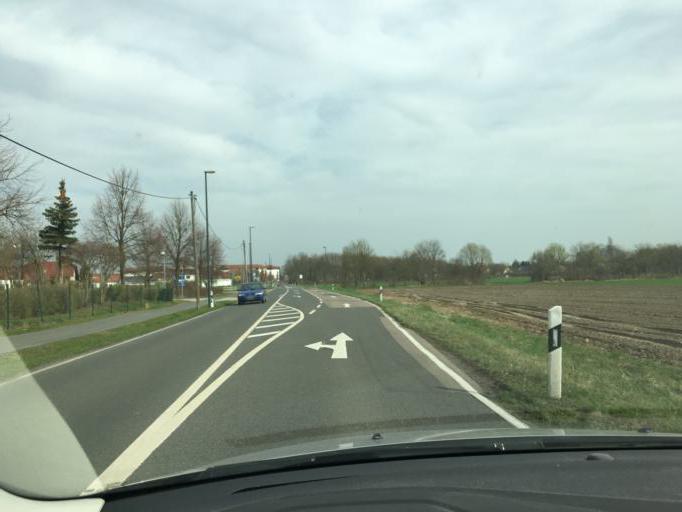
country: DE
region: Saxony
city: Taucha
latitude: 51.3704
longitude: 12.4928
